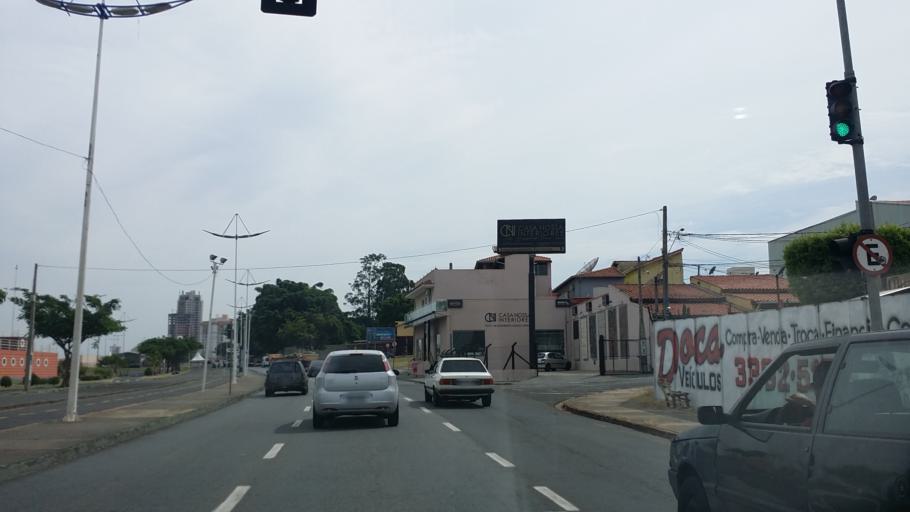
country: BR
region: Sao Paulo
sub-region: Indaiatuba
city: Indaiatuba
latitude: -23.1046
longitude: -47.2274
